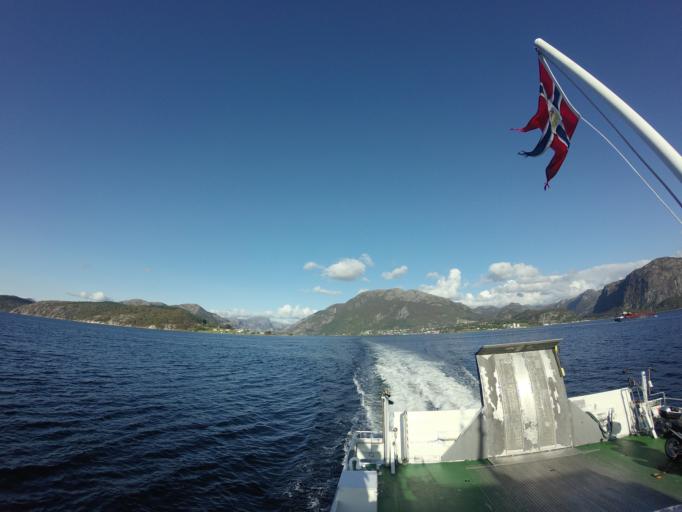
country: NO
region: Rogaland
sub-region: Forsand
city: Forsand
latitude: 58.8960
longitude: 6.0610
